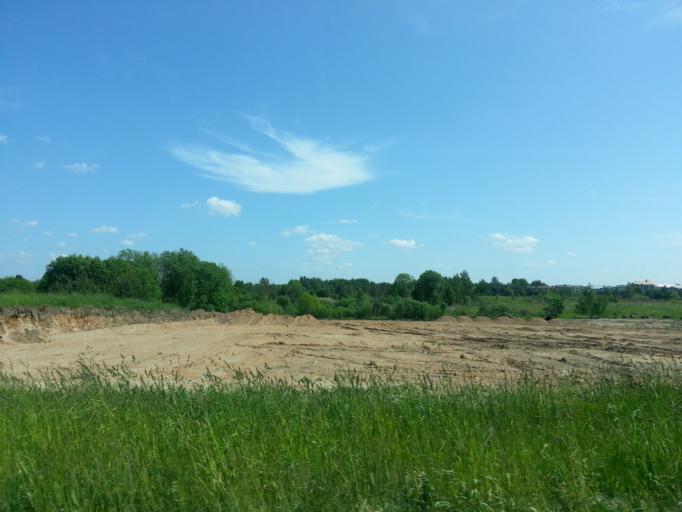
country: LT
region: Vilnius County
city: Pilaite
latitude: 54.7208
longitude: 25.1580
